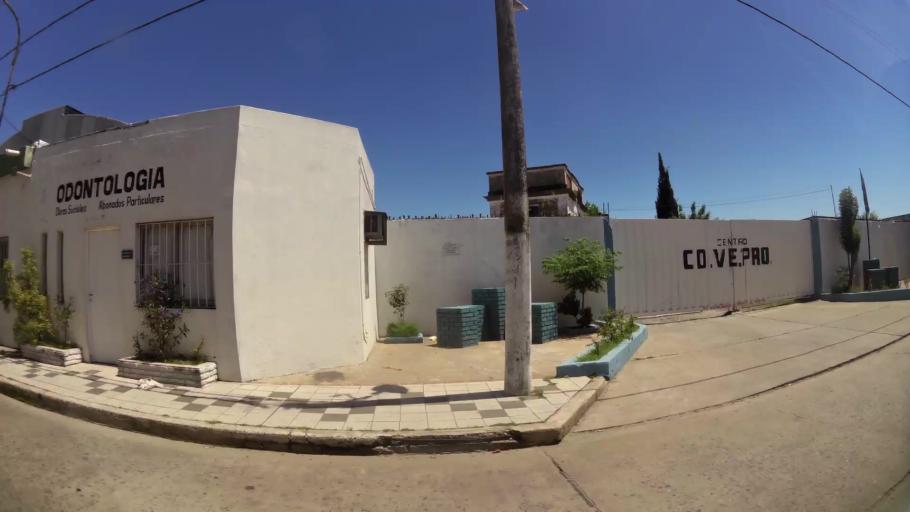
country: AR
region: Santa Fe
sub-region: Departamento de Rosario
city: Rosario
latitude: -32.9435
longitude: -60.7092
